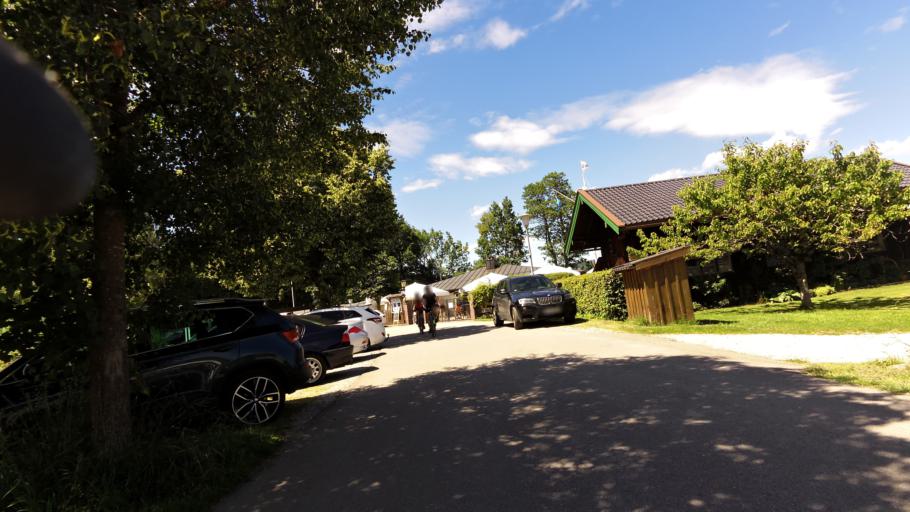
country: DE
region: Bavaria
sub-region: Upper Bavaria
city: Bad Wiessee
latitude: 47.7220
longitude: 11.7255
